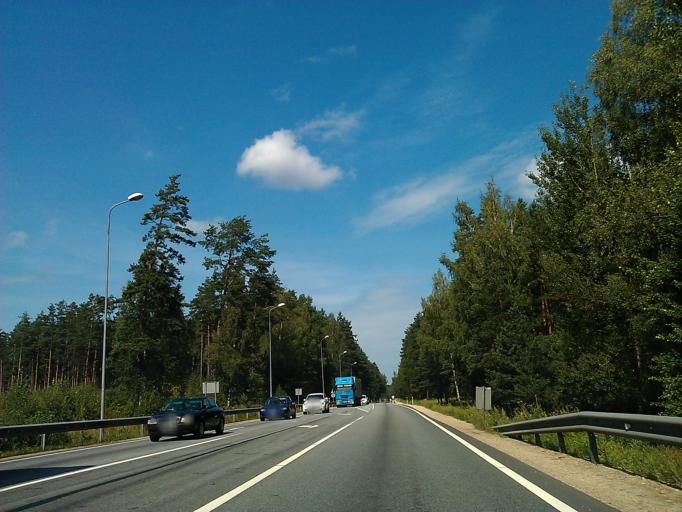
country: LV
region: Salaspils
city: Salaspils
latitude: 56.9431
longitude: 24.3824
